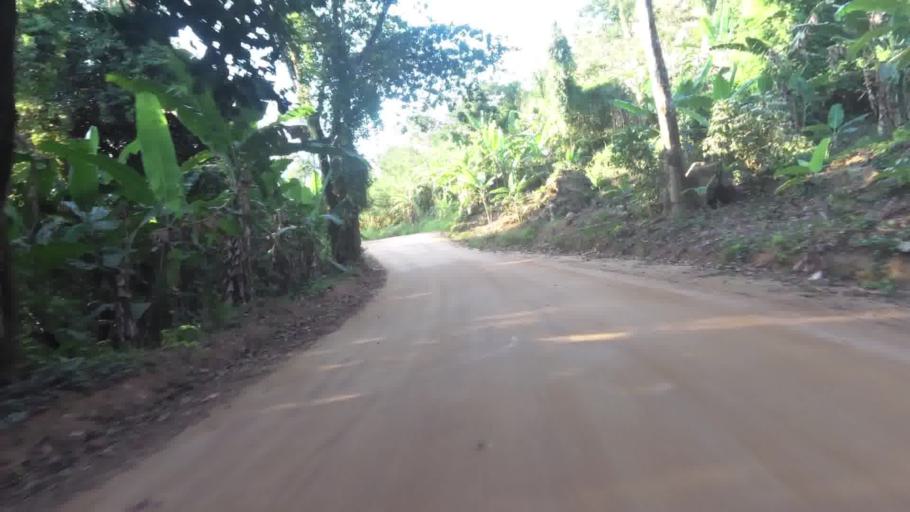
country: BR
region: Espirito Santo
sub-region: Alfredo Chaves
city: Alfredo Chaves
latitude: -20.5941
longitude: -40.6967
